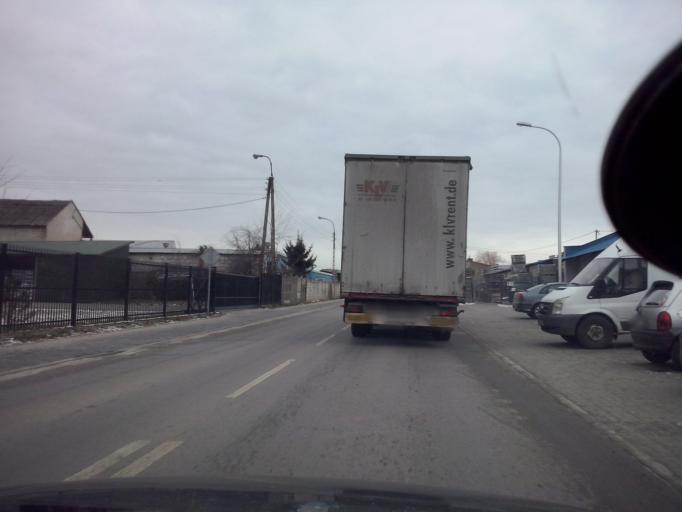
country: PL
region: Lublin Voivodeship
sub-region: Powiat bilgorajski
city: Bilgoraj
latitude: 50.5288
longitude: 22.7255
